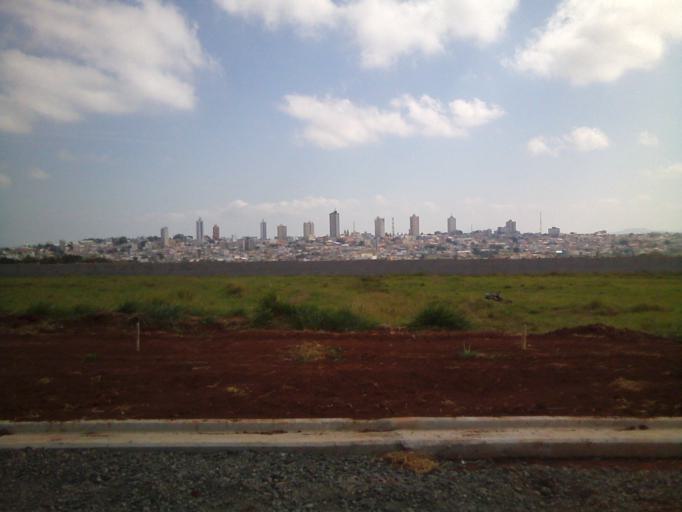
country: BR
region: Minas Gerais
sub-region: Alfenas
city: Alfenas
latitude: -21.4366
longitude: -45.9321
